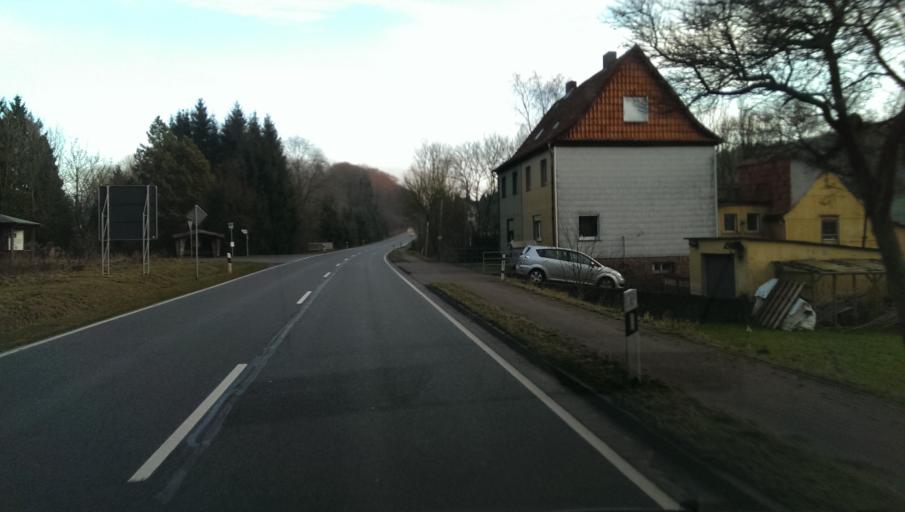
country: DE
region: Lower Saxony
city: Lenne
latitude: 51.9015
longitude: 9.6894
